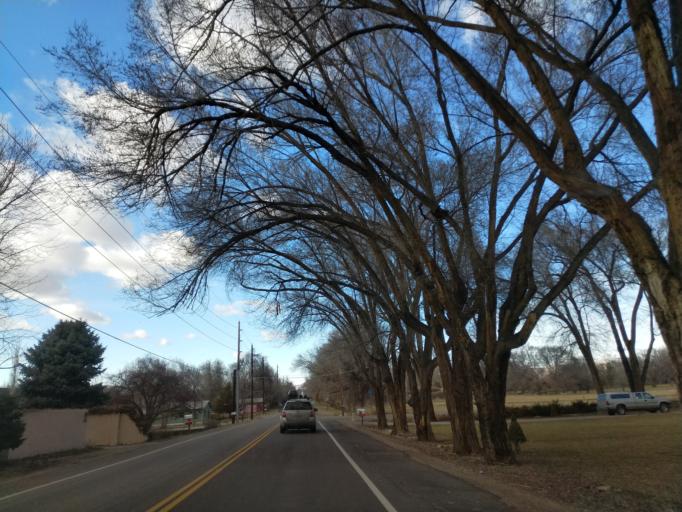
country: US
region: Colorado
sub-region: Mesa County
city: Grand Junction
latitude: 39.0984
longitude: -108.5708
